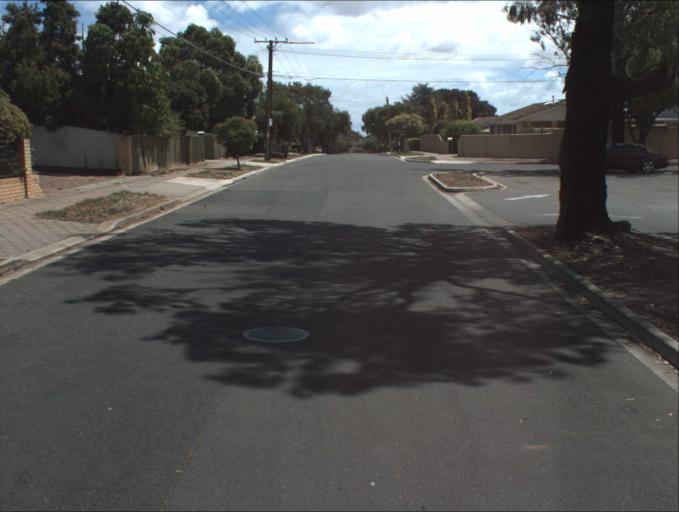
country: AU
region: South Australia
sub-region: Port Adelaide Enfield
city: Gilles Plains
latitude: -34.8434
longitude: 138.6544
